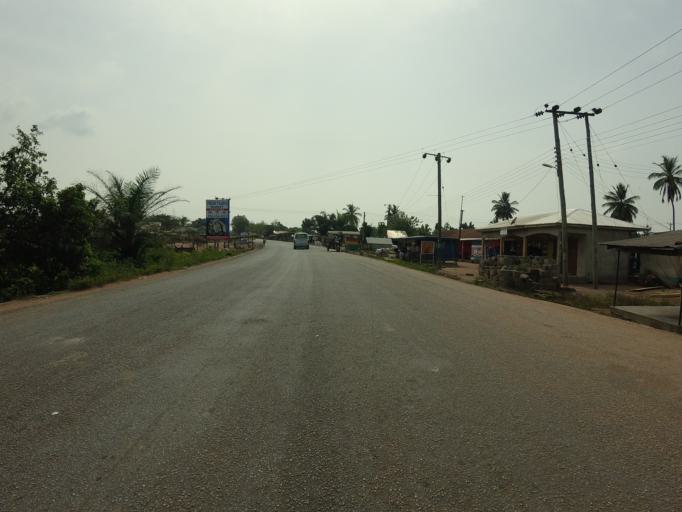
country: GH
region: Volta
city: Ho
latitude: 6.4075
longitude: 0.1732
